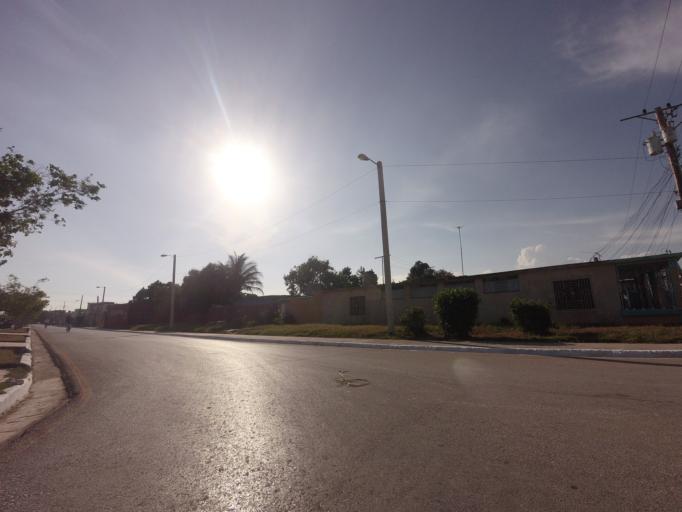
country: CU
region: Ciego de Avila
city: Ciego de Avila
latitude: 21.8466
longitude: -78.7705
